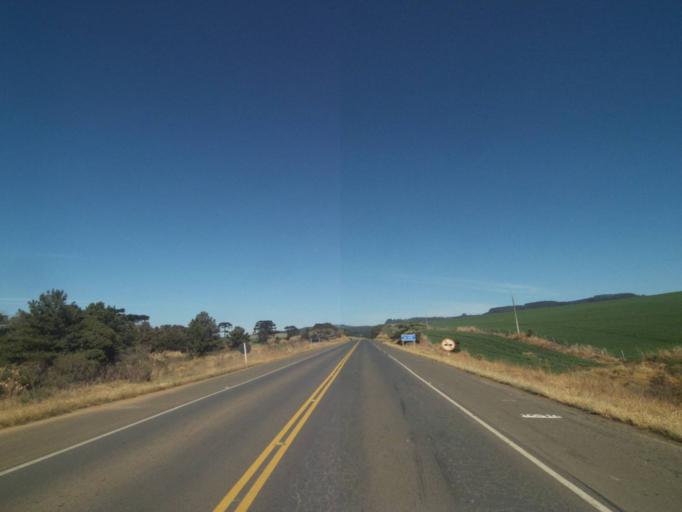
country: BR
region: Parana
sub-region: Tibagi
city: Tibagi
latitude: -24.5413
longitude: -50.4475
